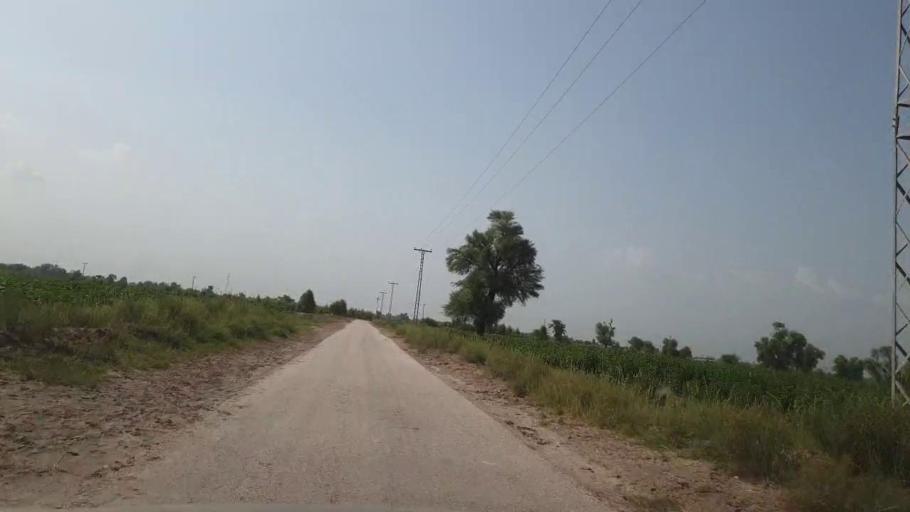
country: PK
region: Sindh
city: Pano Aqil
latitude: 27.7883
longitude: 69.1555
